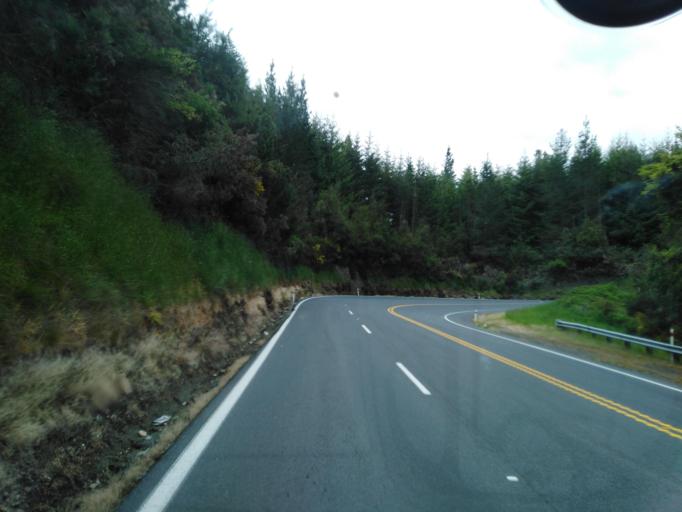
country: NZ
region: Tasman
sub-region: Tasman District
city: Wakefield
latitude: -41.6285
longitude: 172.7257
